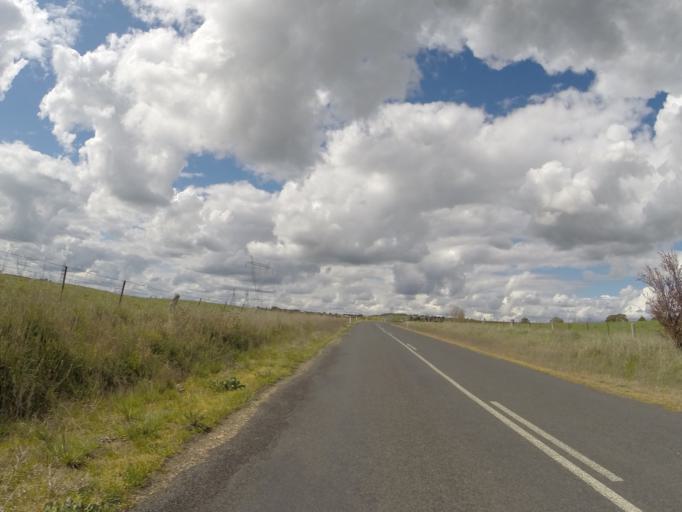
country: AU
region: New South Wales
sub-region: Yass Valley
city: Yass
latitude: -34.8750
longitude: 148.9052
